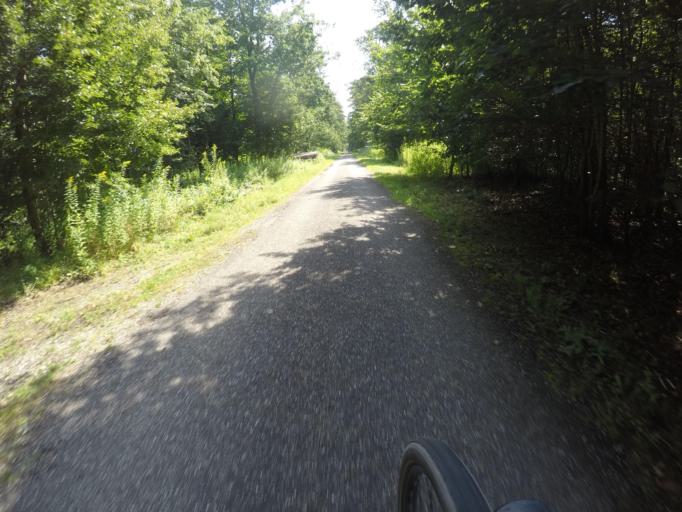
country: DE
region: Baden-Wuerttemberg
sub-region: Karlsruhe Region
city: Kronau
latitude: 49.2131
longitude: 8.5883
